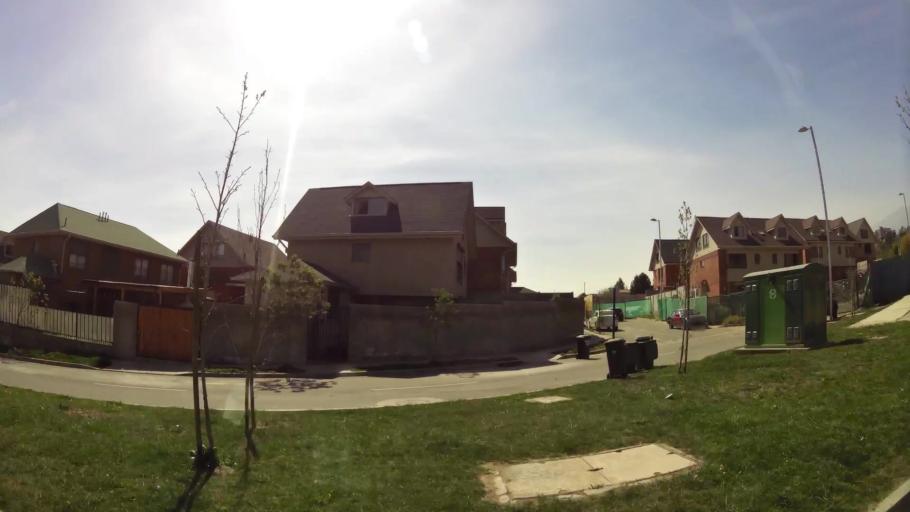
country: CL
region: Santiago Metropolitan
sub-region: Provincia de Cordillera
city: Puente Alto
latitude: -33.5403
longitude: -70.5482
